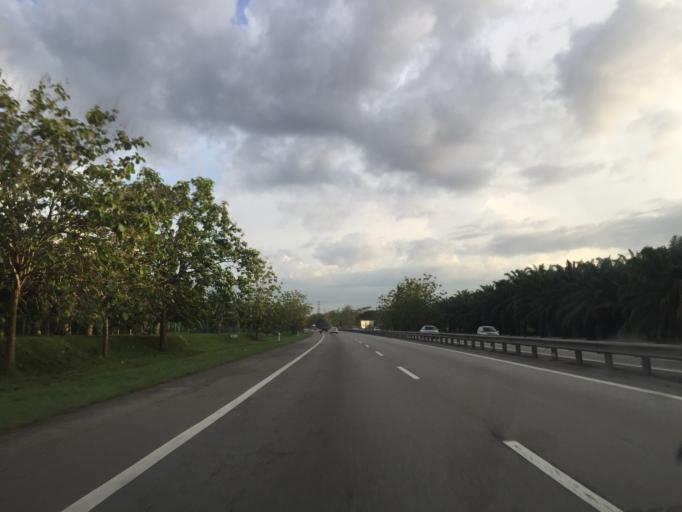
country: MY
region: Kedah
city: Bedong
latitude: 5.7602
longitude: 100.5060
